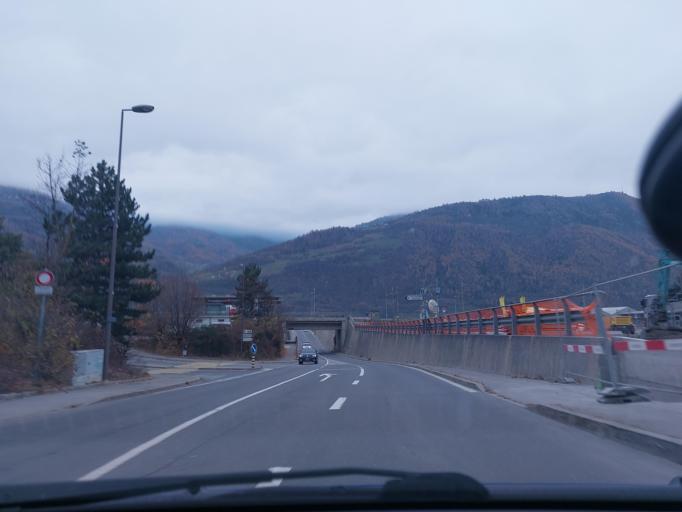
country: CH
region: Valais
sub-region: Conthey District
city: Conthey
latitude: 46.2168
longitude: 7.3041
